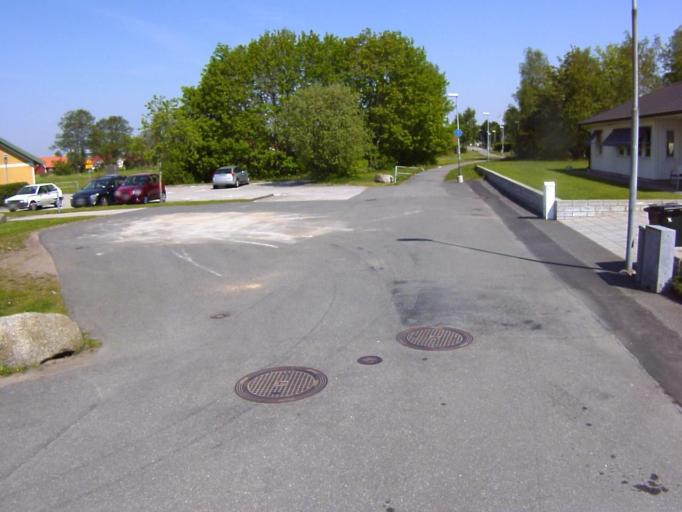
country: SE
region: Skane
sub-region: Kristianstads Kommun
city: Ahus
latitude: 55.9790
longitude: 14.2688
